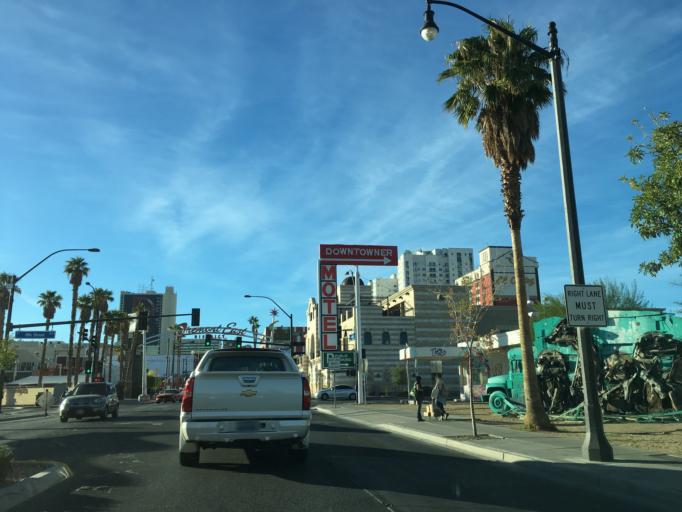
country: US
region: Nevada
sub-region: Clark County
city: Las Vegas
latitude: 36.1676
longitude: -115.1367
